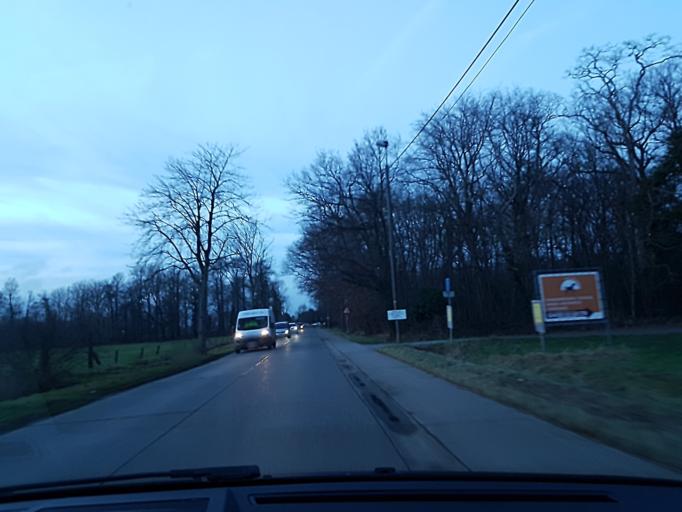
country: BE
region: Flanders
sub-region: Provincie Vlaams-Brabant
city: Boortmeerbeek
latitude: 50.9949
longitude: 4.5902
